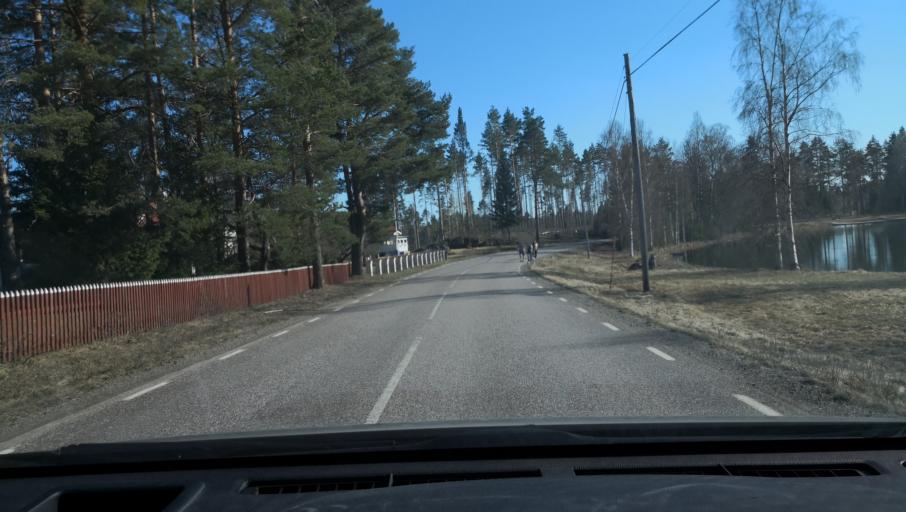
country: SE
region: Dalarna
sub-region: Avesta Kommun
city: Avesta
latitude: 59.9999
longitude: 16.3473
